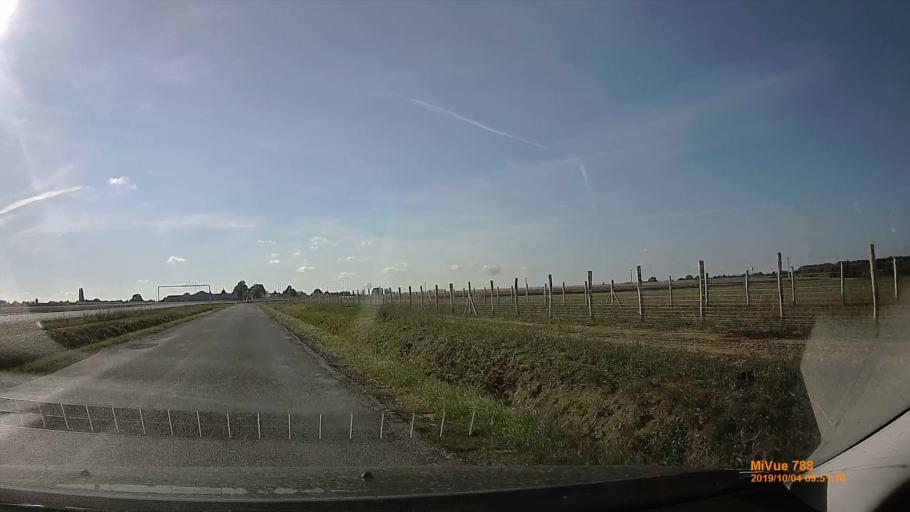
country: HU
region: Somogy
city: Kaposvar
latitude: 46.4281
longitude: 17.7734
